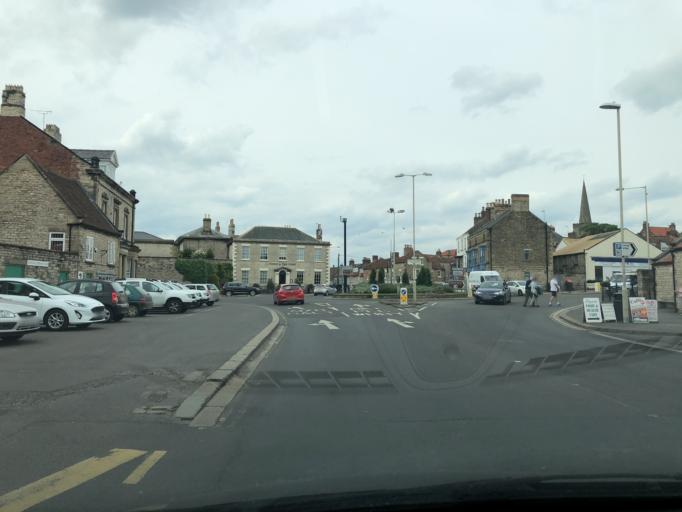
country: GB
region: England
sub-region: North Yorkshire
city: Pickering
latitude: 54.2436
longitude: -0.7744
